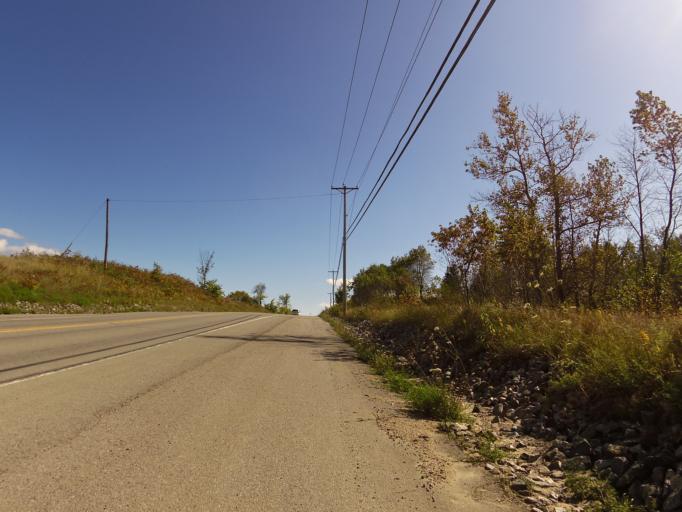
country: CA
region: Ontario
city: Clarence-Rockland
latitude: 45.6478
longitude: -75.4414
